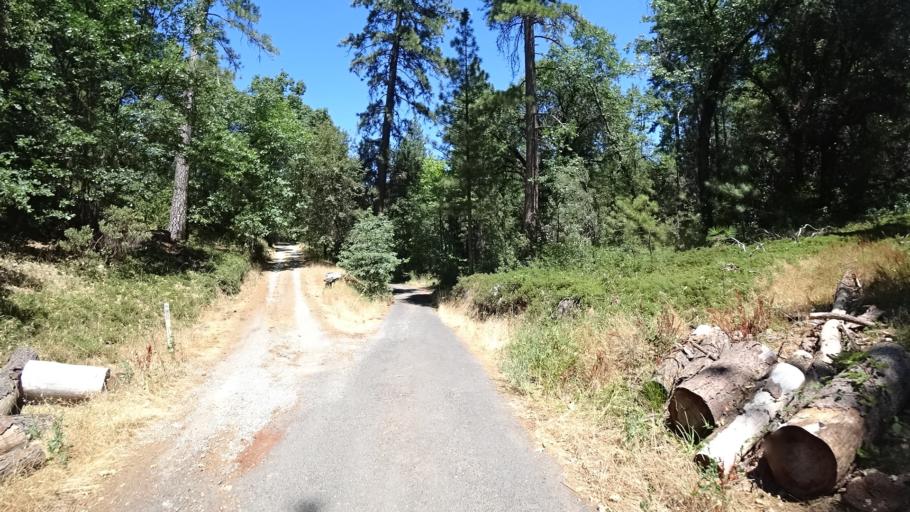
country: US
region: California
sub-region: Calaveras County
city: Forest Meadows
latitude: 38.1544
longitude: -120.4014
